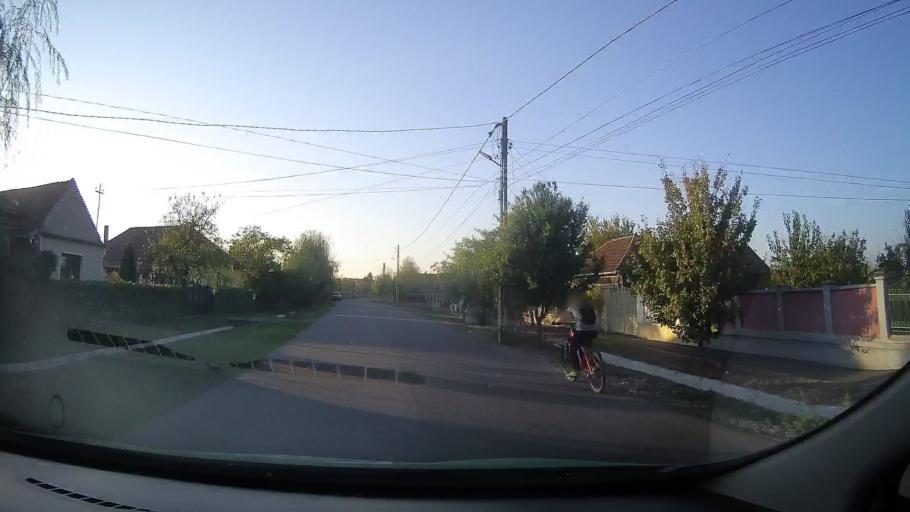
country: RO
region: Bihor
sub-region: Comuna Salard
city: Salard
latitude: 47.2230
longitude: 22.0342
